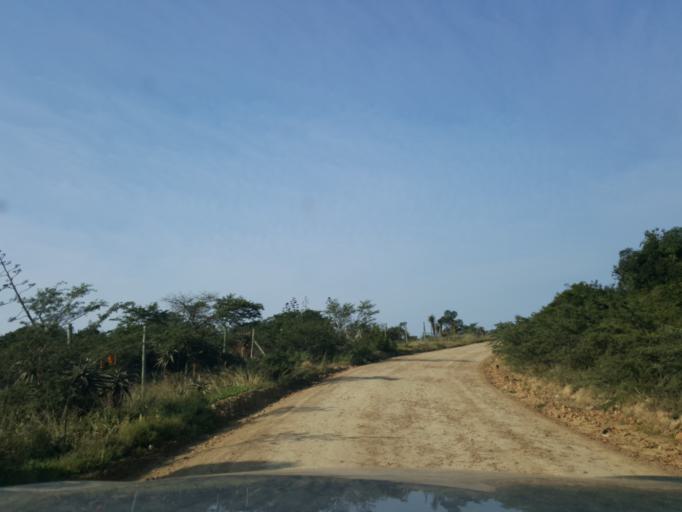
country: ZA
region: Eastern Cape
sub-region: Cacadu District Municipality
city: Grahamstown
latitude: -33.4166
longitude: 26.3167
